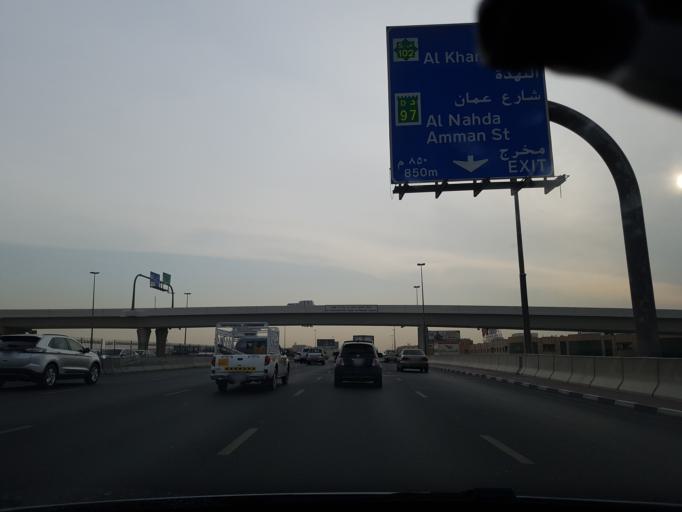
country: AE
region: Ash Shariqah
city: Sharjah
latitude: 25.2971
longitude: 55.4373
